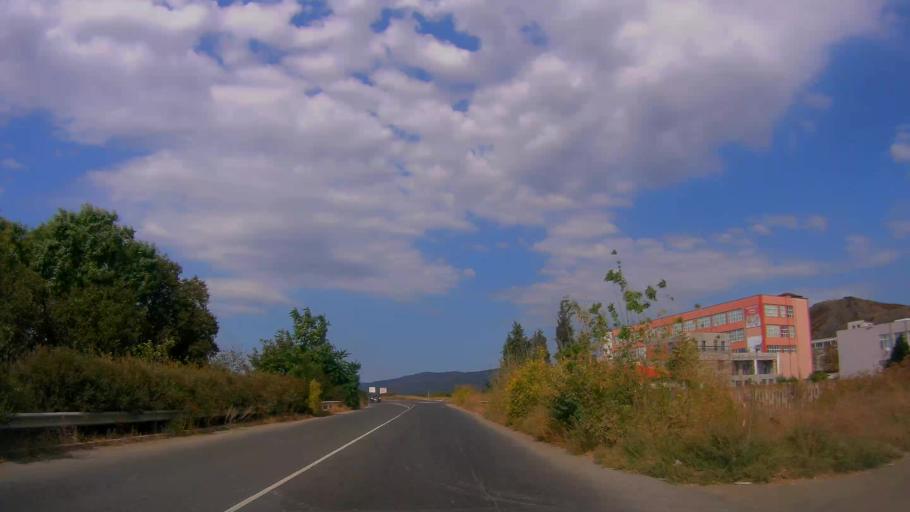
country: BG
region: Burgas
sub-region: Obshtina Aytos
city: Aytos
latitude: 42.7031
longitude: 27.2443
